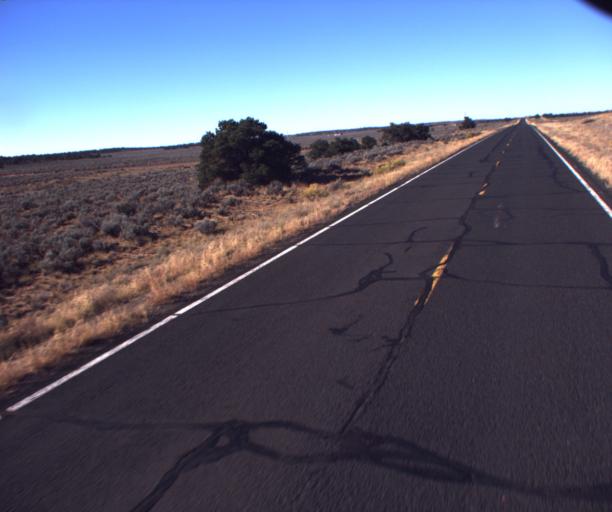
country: US
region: Arizona
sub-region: Navajo County
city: First Mesa
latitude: 35.7390
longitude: -110.0799
